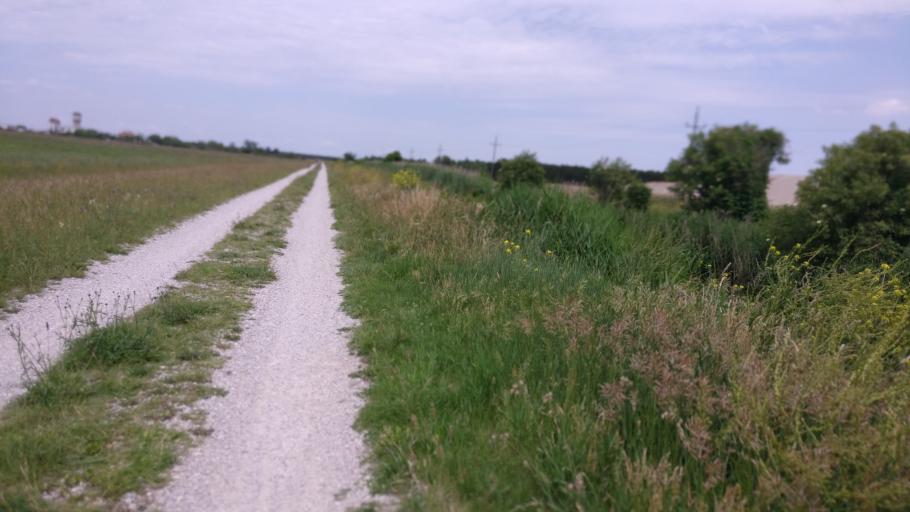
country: AT
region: Lower Austria
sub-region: Politischer Bezirk Wiener Neustadt
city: Lichtenworth
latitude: 47.8463
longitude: 16.2757
